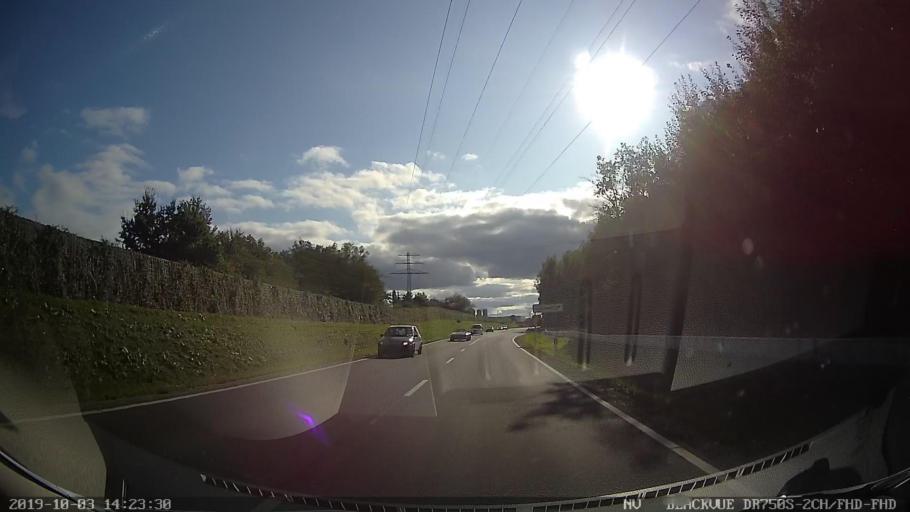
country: DE
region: Schleswig-Holstein
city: Pinneberg
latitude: 53.6724
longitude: 9.7821
